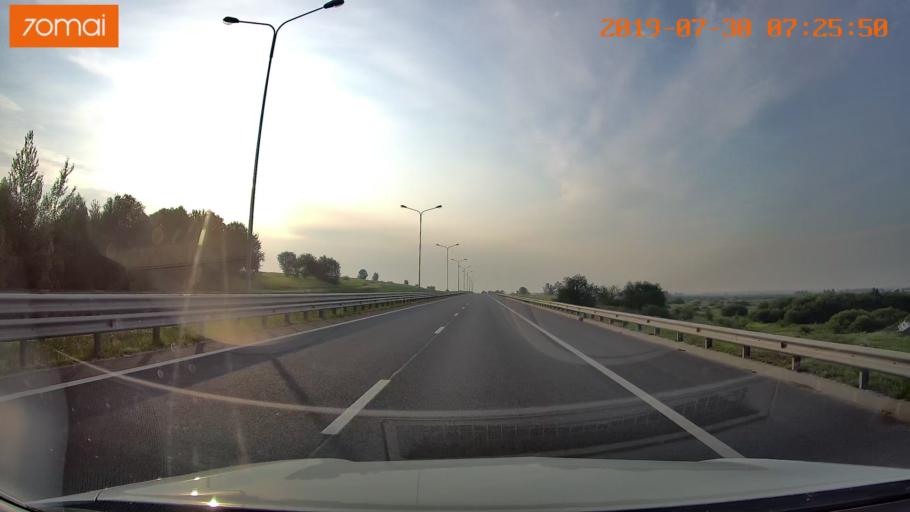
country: RU
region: Kaliningrad
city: Gvardeysk
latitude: 54.6850
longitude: 20.8444
